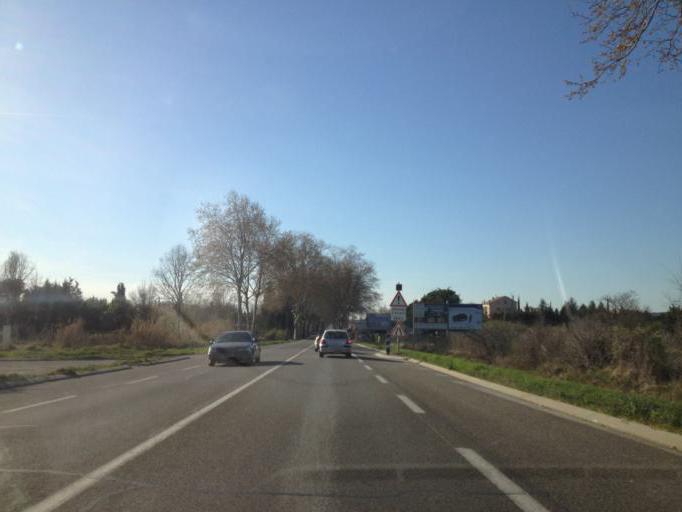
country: FR
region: Provence-Alpes-Cote d'Azur
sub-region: Departement des Bouches-du-Rhone
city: Eguilles
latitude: 43.5661
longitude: 5.4026
